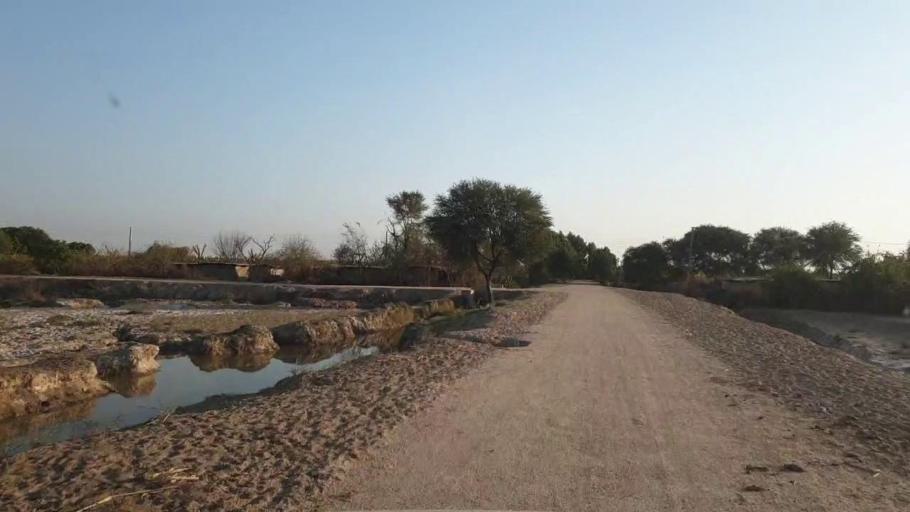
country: PK
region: Sindh
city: Tando Allahyar
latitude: 25.3336
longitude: 68.6822
